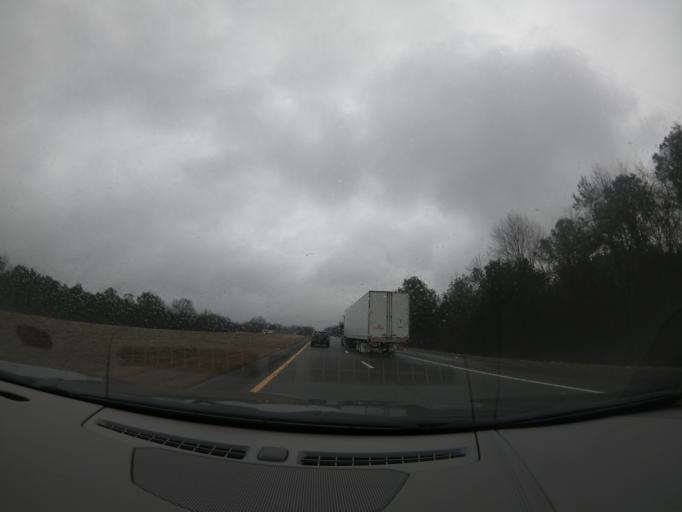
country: US
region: Tennessee
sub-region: Rutherford County
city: Plainview
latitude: 35.7117
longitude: -86.3128
